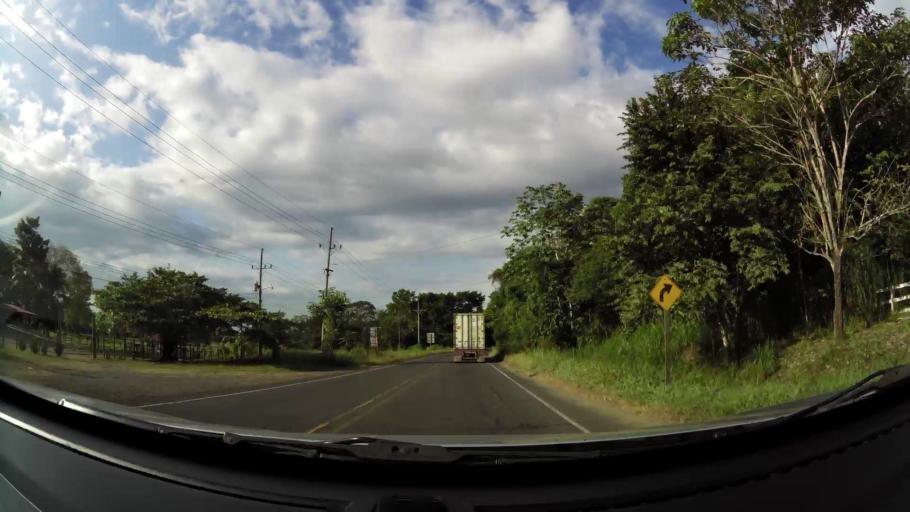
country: CR
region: Alajuela
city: Orotina
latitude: 9.7811
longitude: -84.6069
